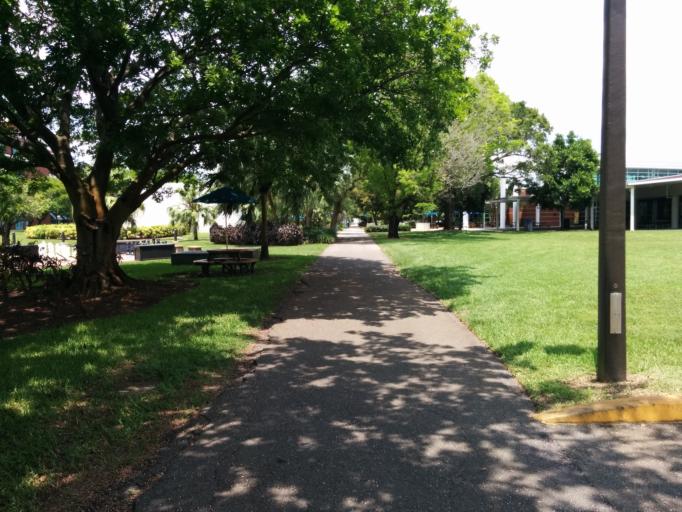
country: US
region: Florida
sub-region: Broward County
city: Davie
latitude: 26.0787
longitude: -80.2347
